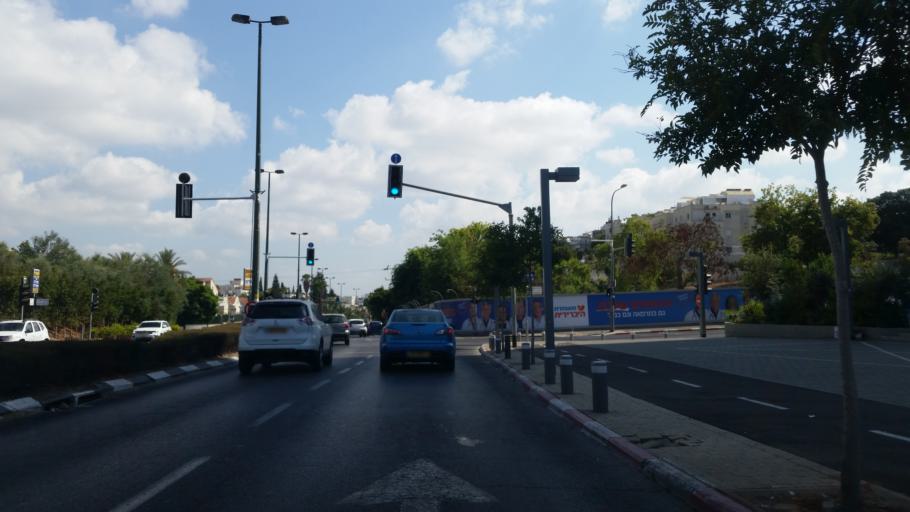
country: IL
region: Tel Aviv
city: Ramat HaSharon
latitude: 32.1233
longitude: 34.8243
